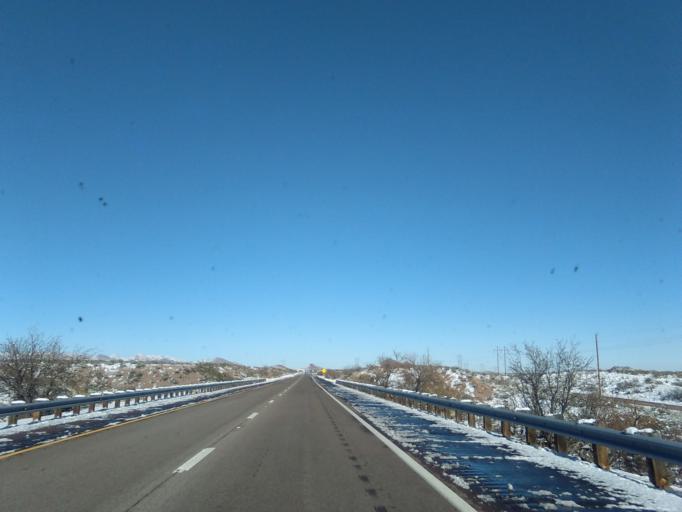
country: US
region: New Mexico
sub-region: Socorro County
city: Socorro
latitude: 33.7094
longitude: -107.0403
